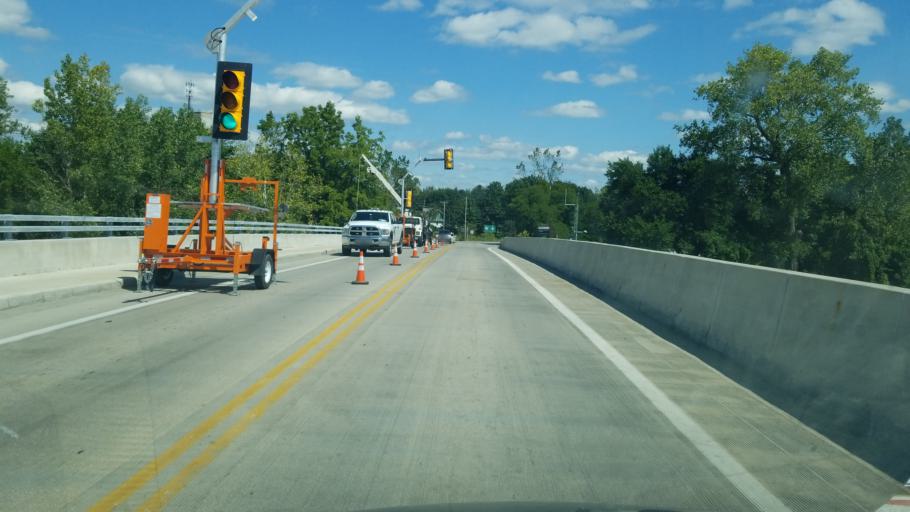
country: US
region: Ohio
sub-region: Wood County
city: Weston
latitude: 41.4145
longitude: -83.8607
